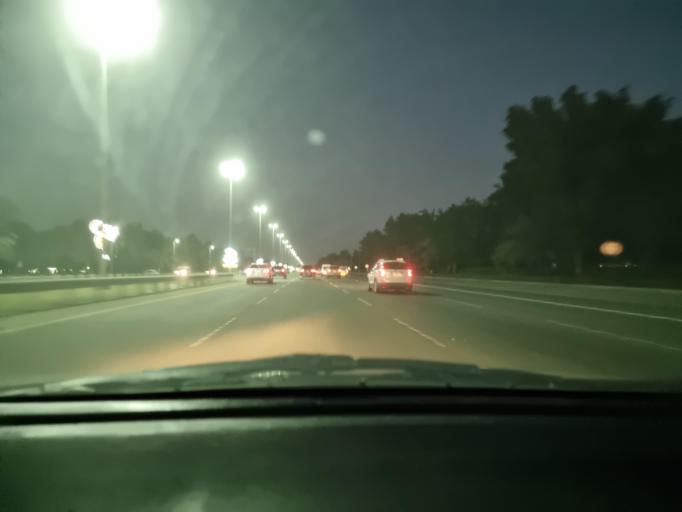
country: AE
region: Abu Dhabi
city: Abu Dhabi
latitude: 24.4008
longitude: 54.5913
